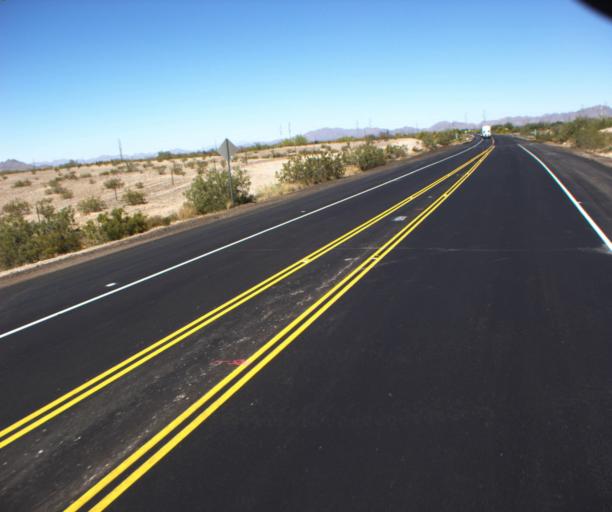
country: US
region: Arizona
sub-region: Maricopa County
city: Gila Bend
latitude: 32.9632
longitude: -112.6775
